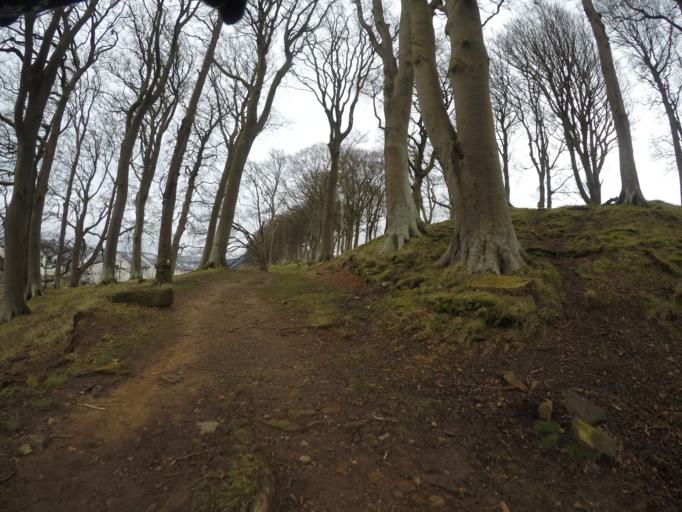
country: GB
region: Scotland
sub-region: North Ayrshire
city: Fairlie
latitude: 55.7576
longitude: -4.8498
